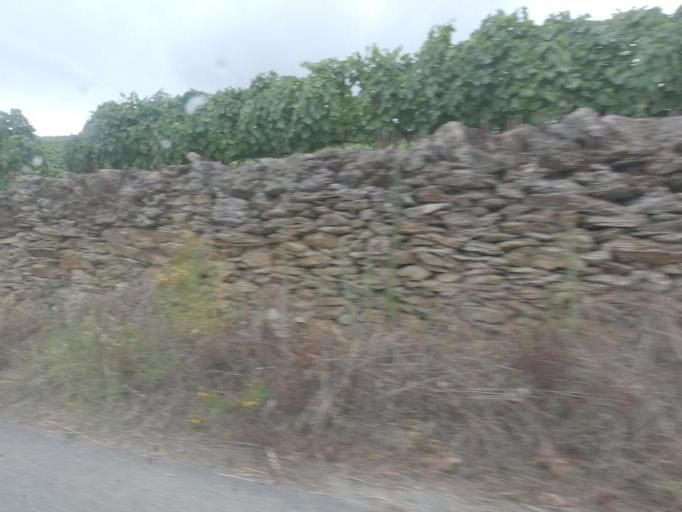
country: PT
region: Vila Real
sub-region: Sabrosa
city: Sabrosa
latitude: 41.2311
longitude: -7.4982
